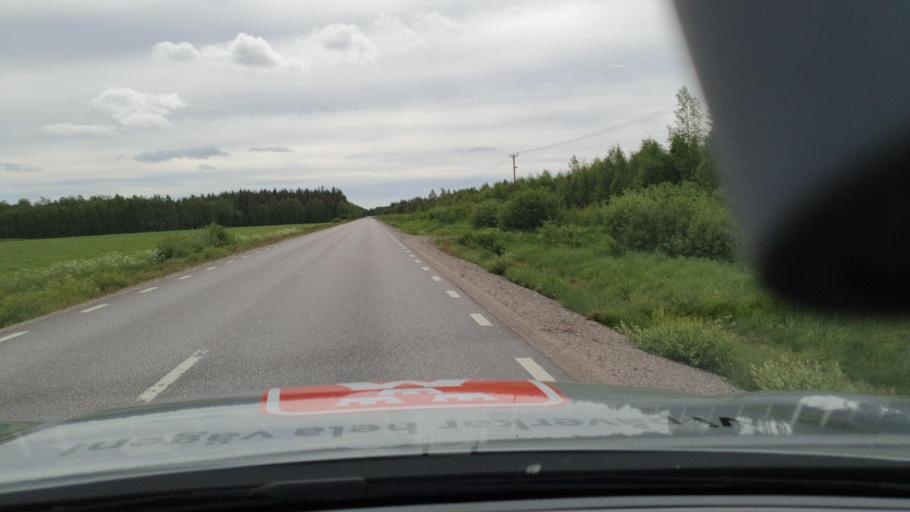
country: SE
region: Norrbotten
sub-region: Kalix Kommun
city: Kalix
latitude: 65.8853
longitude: 23.4744
